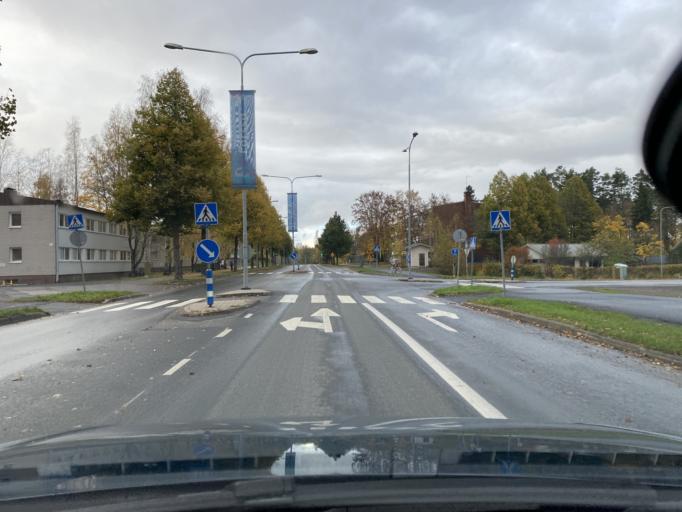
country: FI
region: Haeme
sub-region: Forssa
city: Forssa
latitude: 60.8197
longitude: 23.6089
